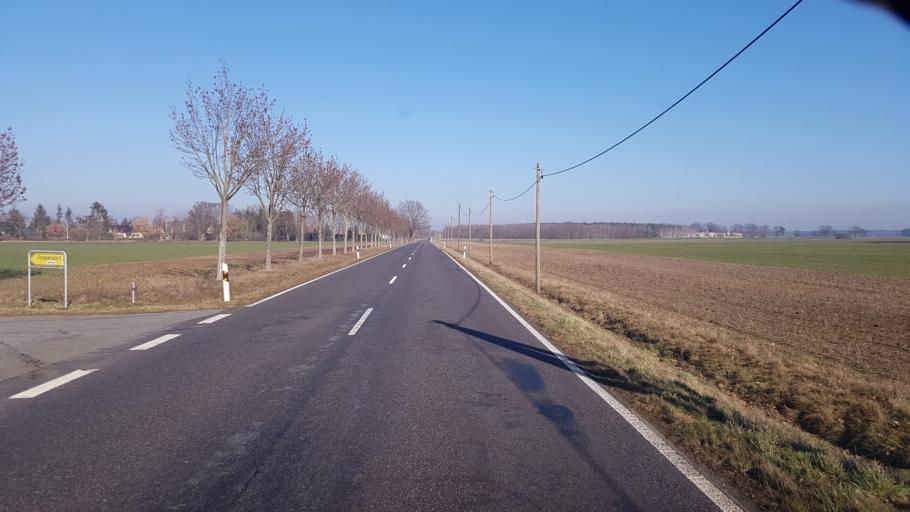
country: DE
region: Brandenburg
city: Ihlow
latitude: 51.8129
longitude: 13.3333
